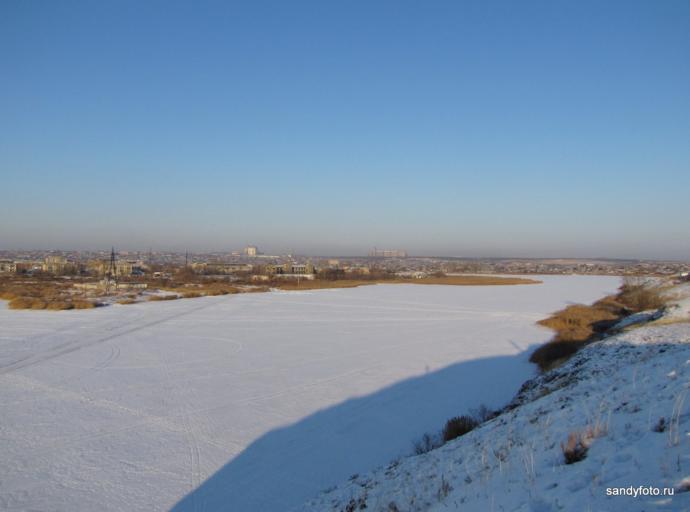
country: RU
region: Chelyabinsk
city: Troitsk
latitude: 54.0783
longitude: 61.5782
